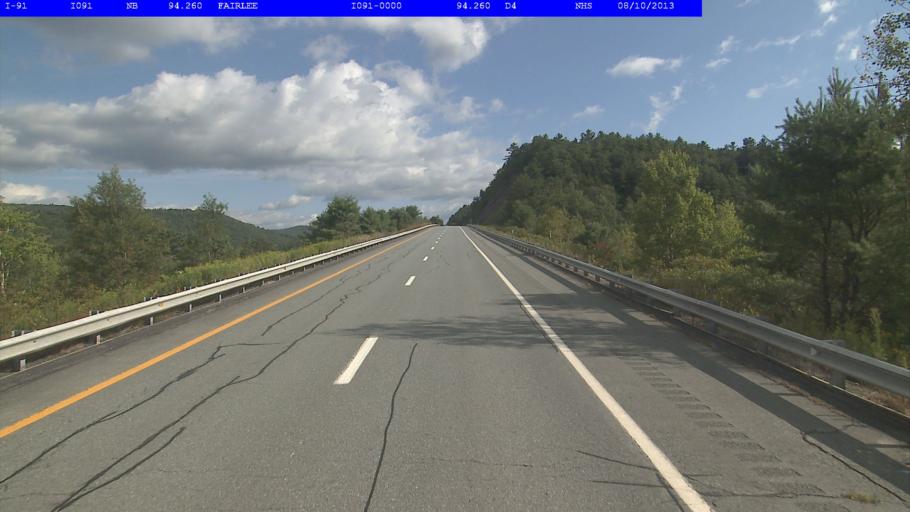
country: US
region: New Hampshire
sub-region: Grafton County
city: Orford
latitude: 43.9367
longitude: -72.1331
